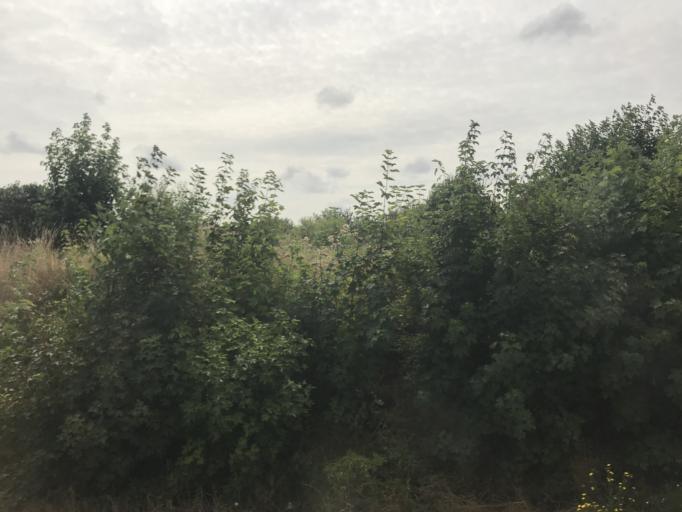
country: PL
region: Kujawsko-Pomorskie
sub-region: Powiat inowroclawski
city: Janikowo
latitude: 52.7249
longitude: 18.0625
